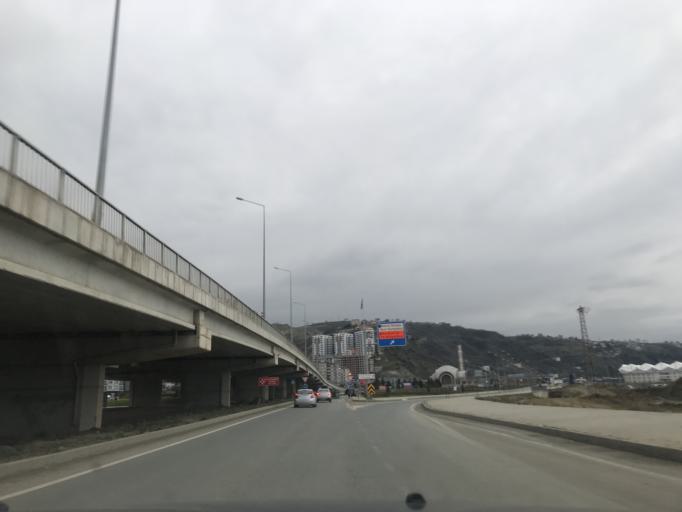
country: TR
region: Trabzon
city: Trabzon
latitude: 40.9958
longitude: 39.6644
